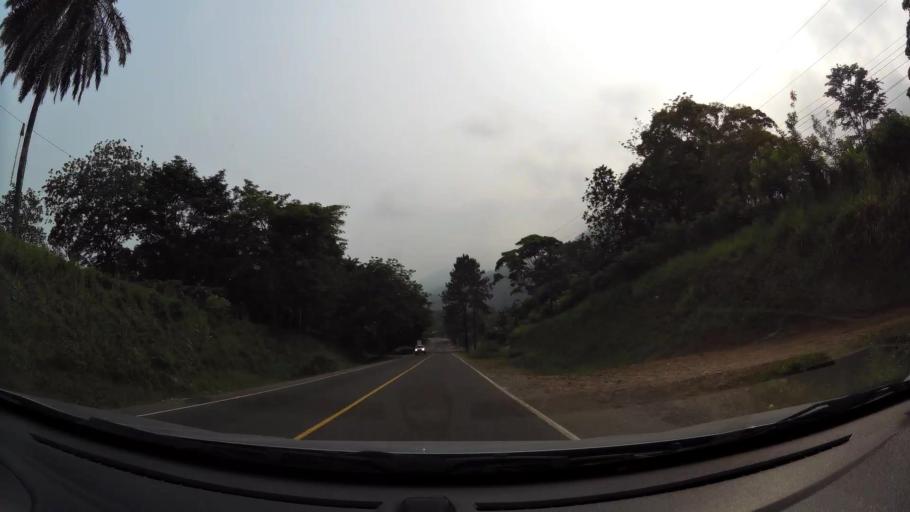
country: HN
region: Atlantida
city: Mezapa
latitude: 15.5910
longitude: -87.6105
